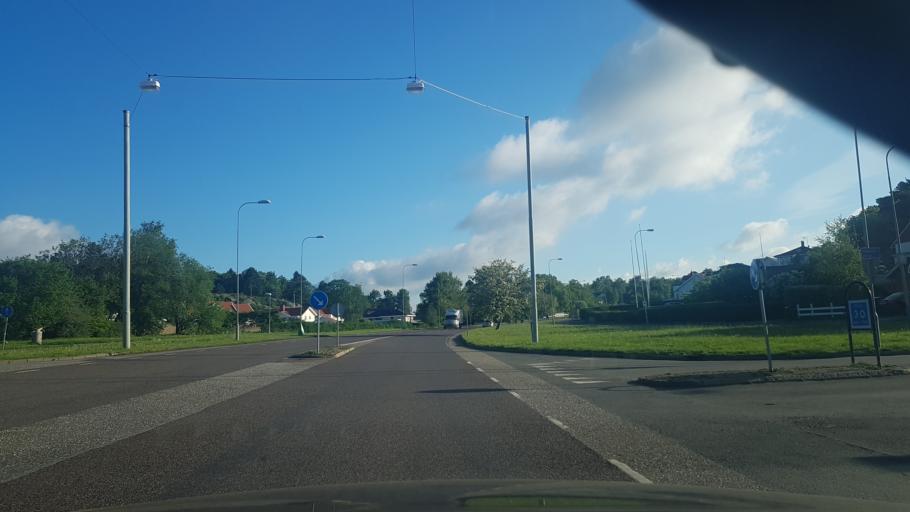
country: SE
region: Vaestra Goetaland
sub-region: Goteborg
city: Majorna
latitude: 57.6431
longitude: 11.8806
